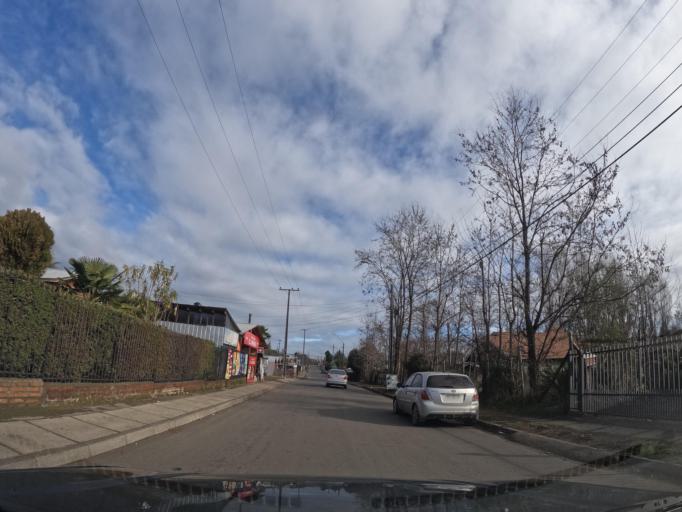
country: CL
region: Biobio
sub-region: Provincia de Nuble
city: Coihueco
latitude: -36.6994
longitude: -71.8975
